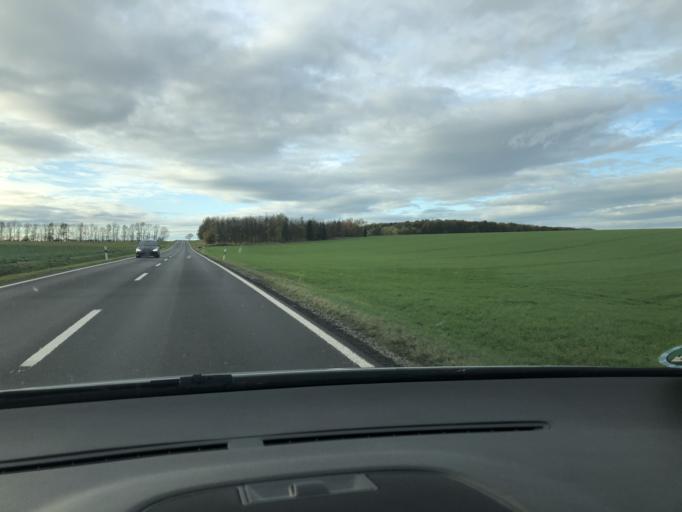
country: DE
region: Thuringia
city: Frankendorf
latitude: 50.9680
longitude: 11.4424
